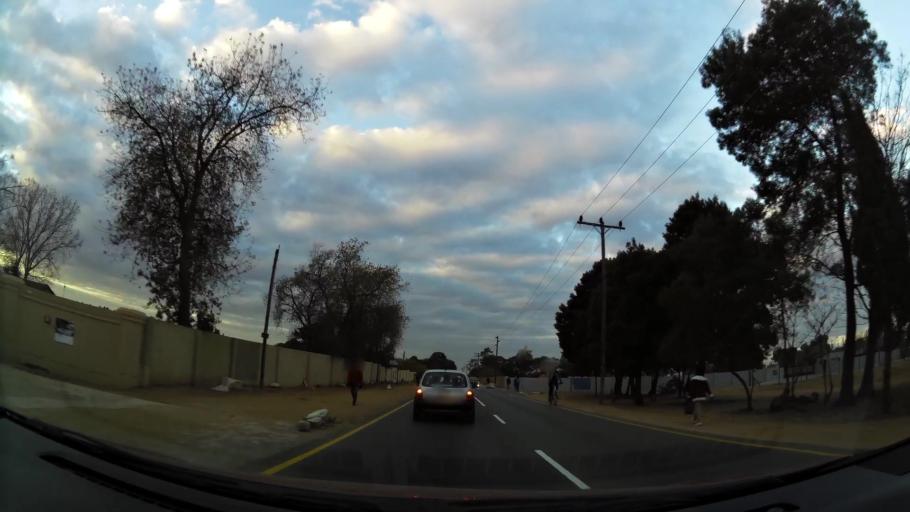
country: ZA
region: Gauteng
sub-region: City of Johannesburg Metropolitan Municipality
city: Midrand
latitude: -25.9877
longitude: 28.1549
